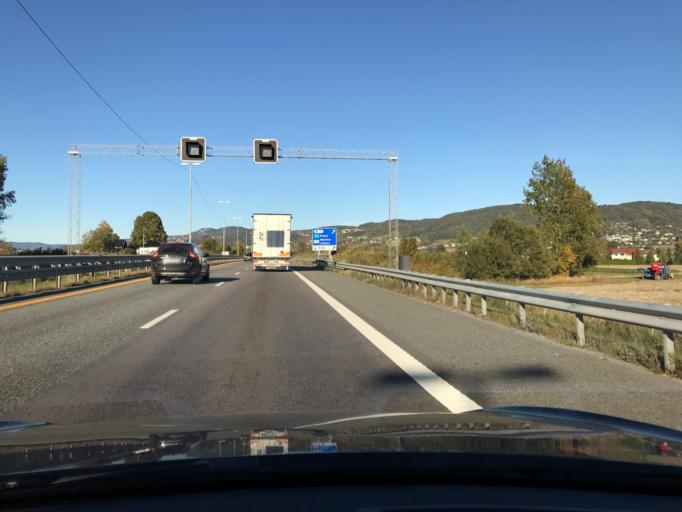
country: NO
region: Buskerud
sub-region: Lier
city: Lierbyen
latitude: 59.7601
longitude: 10.2516
